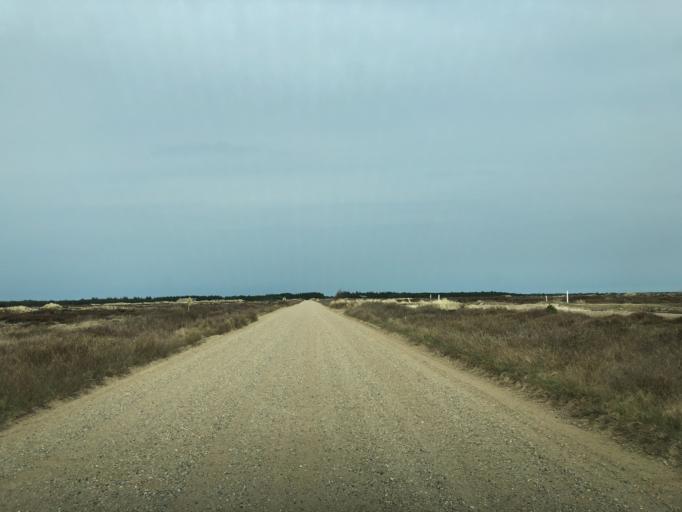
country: DK
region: South Denmark
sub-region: Varde Kommune
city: Oksbol
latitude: 55.5933
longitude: 8.1517
